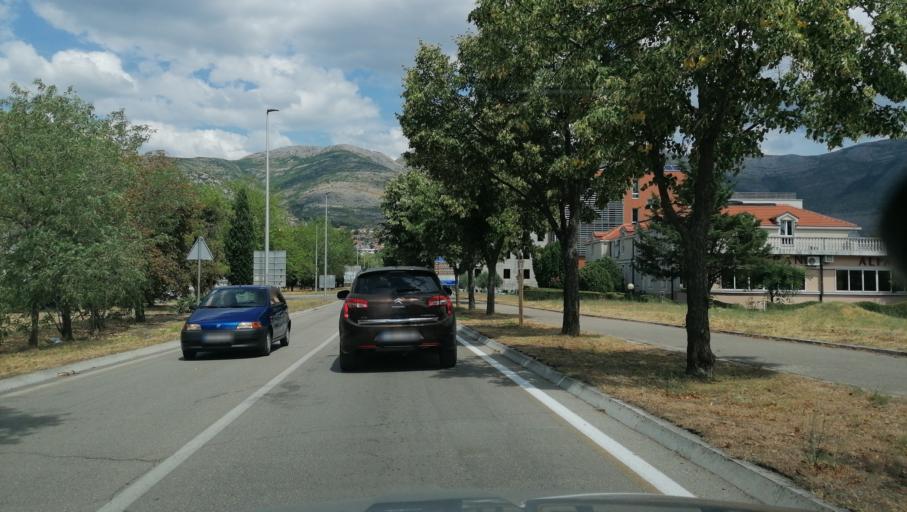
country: BA
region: Republika Srpska
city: Trebinje
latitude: 42.7060
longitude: 18.3428
